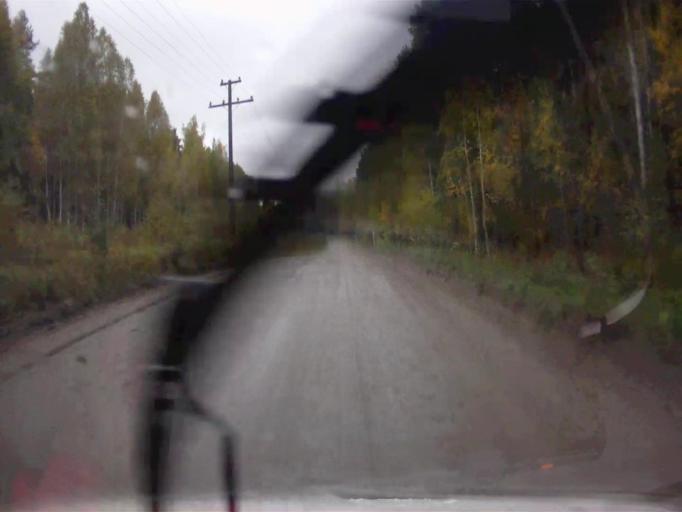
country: RU
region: Chelyabinsk
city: Kyshtym
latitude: 55.8028
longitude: 60.4798
